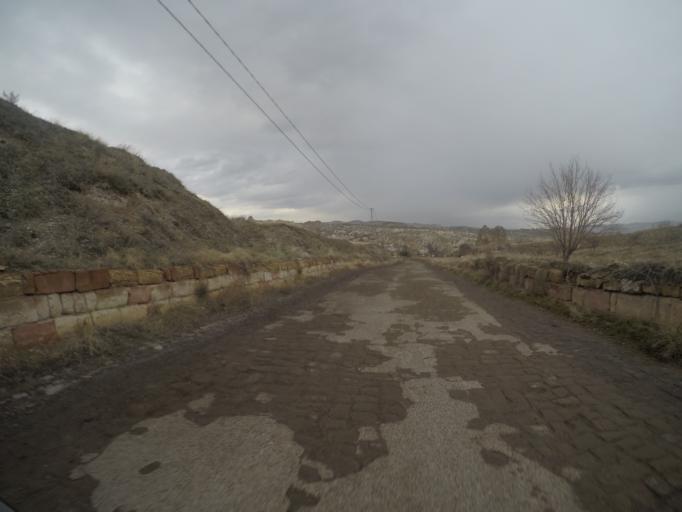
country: TR
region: Nevsehir
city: Goereme
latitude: 38.6171
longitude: 34.8672
